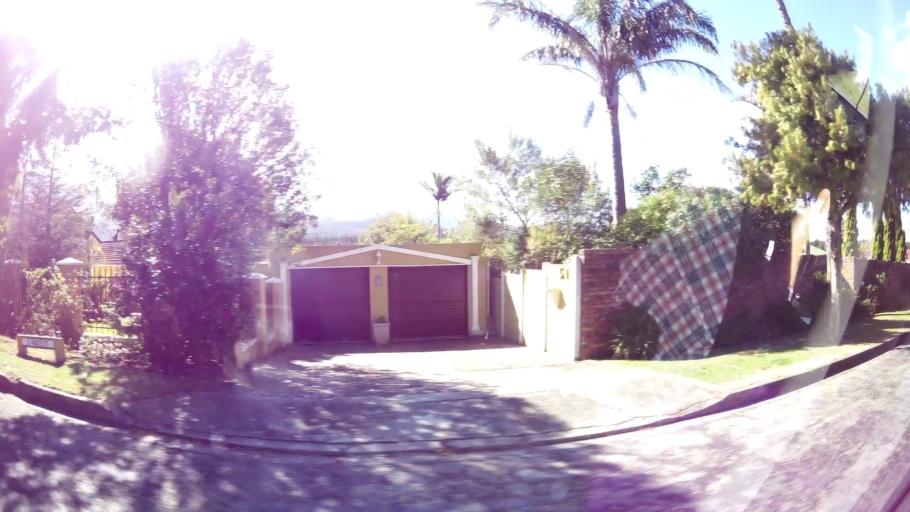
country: ZA
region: Western Cape
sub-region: Eden District Municipality
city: George
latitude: -33.9534
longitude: 22.4819
